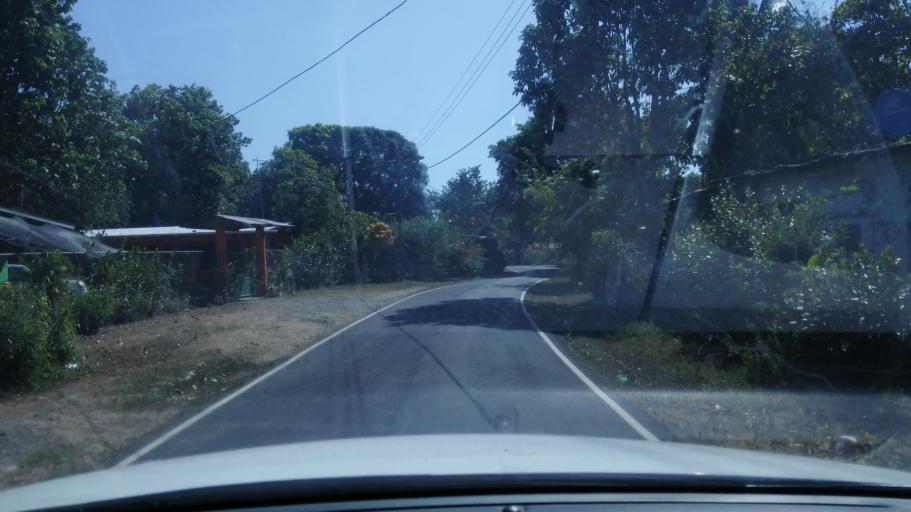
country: PA
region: Chiriqui
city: San Felix
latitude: 8.2919
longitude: -81.8703
